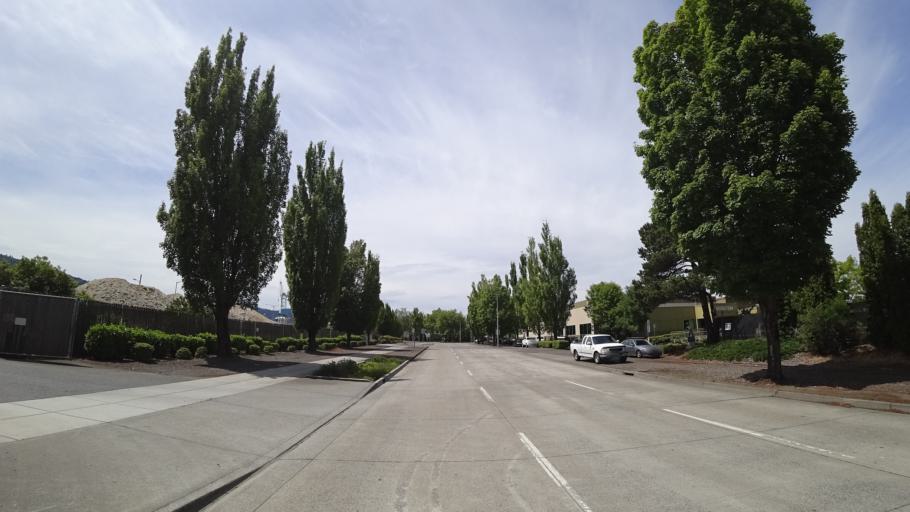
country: US
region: Oregon
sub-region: Multnomah County
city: Portland
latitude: 45.5616
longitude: -122.7142
